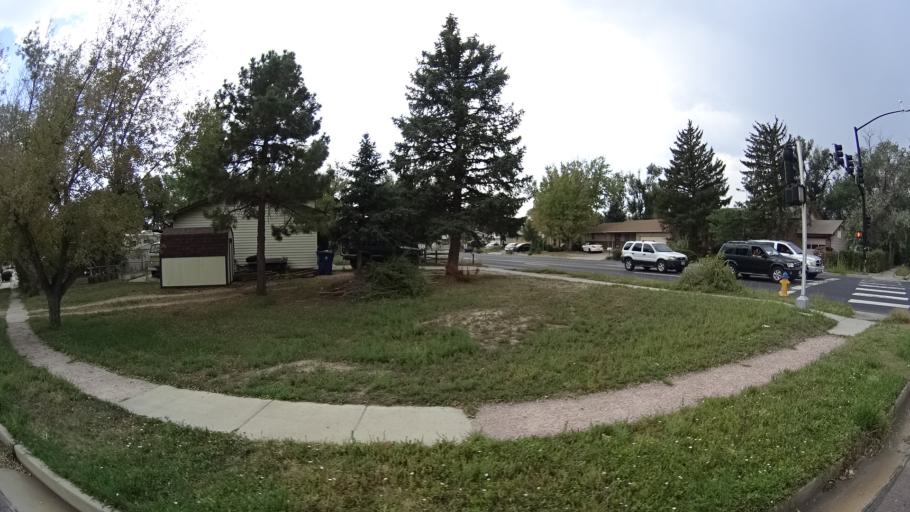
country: US
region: Colorado
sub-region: El Paso County
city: Cimarron Hills
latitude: 38.8507
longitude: -104.7477
